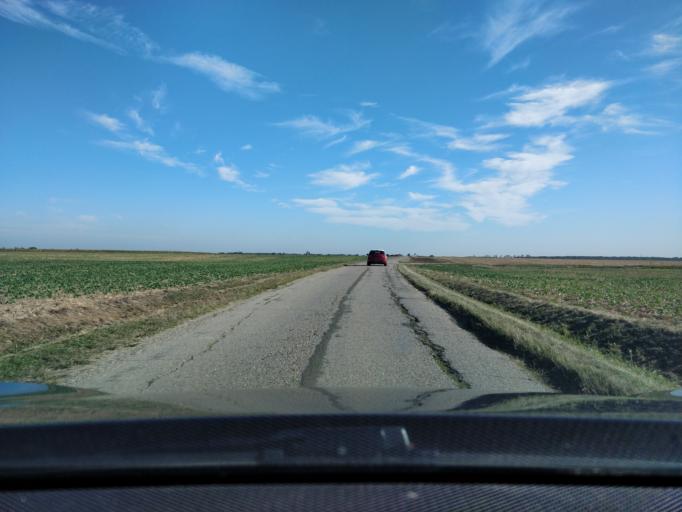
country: FR
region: Ile-de-France
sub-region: Departement de l'Essonne
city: Forges-les-Bains
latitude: 48.6514
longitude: 2.1073
